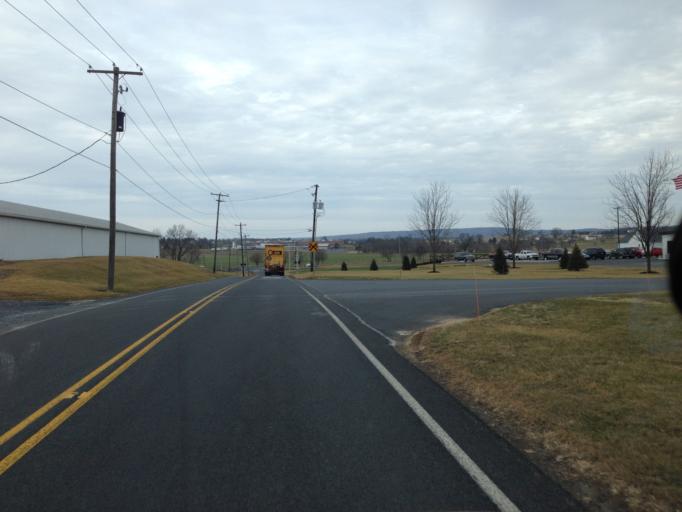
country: US
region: Pennsylvania
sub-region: Lancaster County
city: Manheim
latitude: 40.1640
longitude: -76.3673
